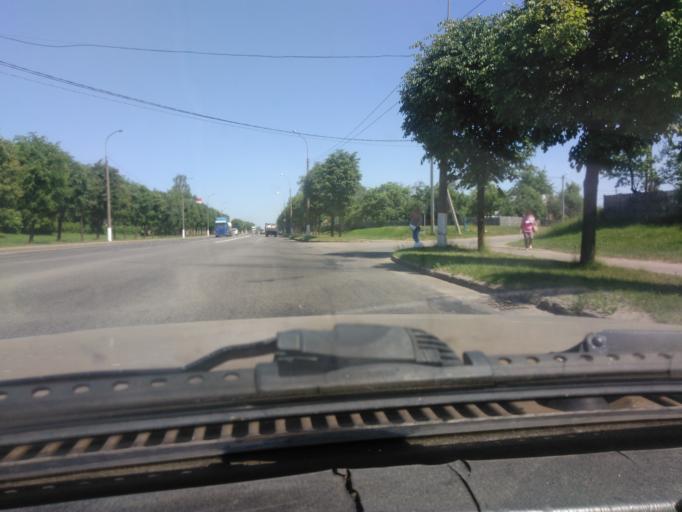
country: BY
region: Mogilev
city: Mahilyow
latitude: 53.9107
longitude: 30.3618
